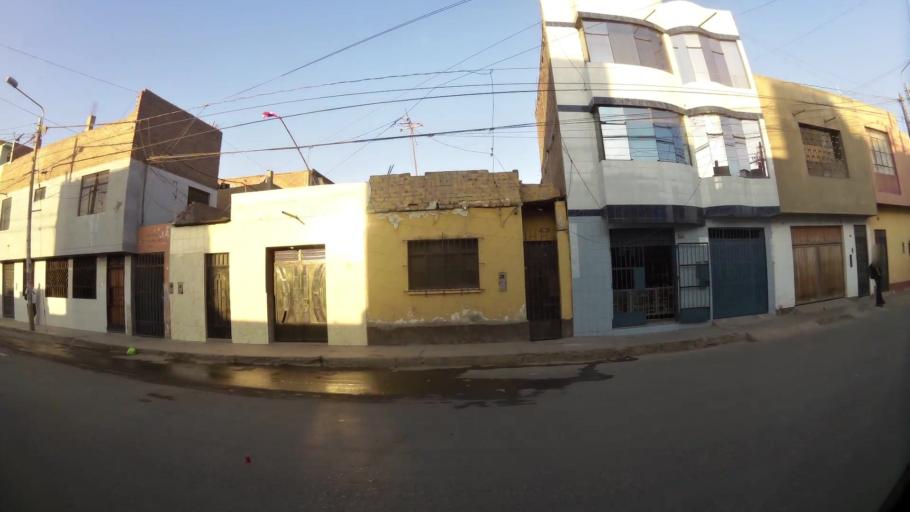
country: PE
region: Lambayeque
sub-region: Provincia de Chiclayo
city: Santa Rosa
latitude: -6.7707
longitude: -79.8318
